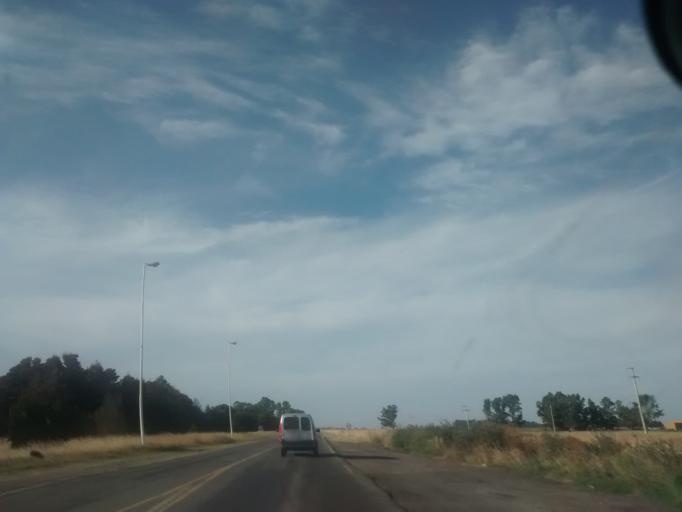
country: AR
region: Buenos Aires
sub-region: Partido de Ayacucho
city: Ayacucho
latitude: -37.1250
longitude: -58.5510
